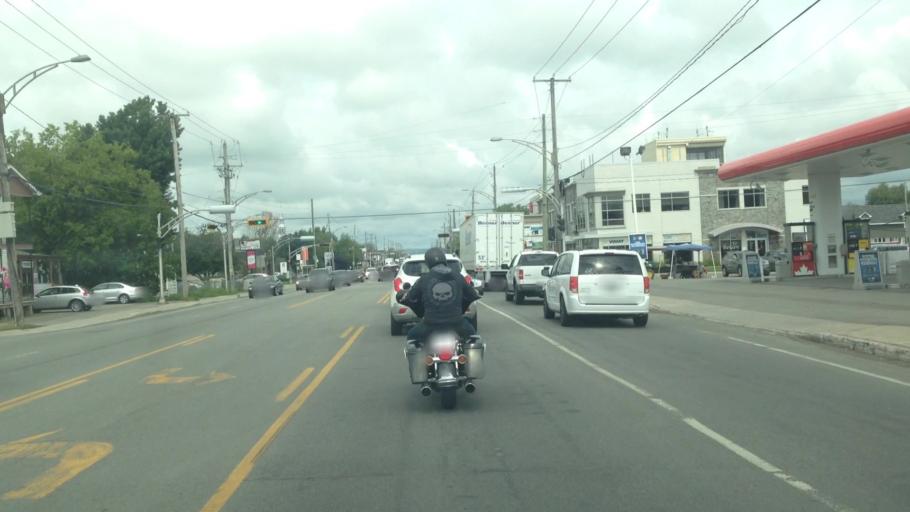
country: CA
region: Quebec
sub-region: Laurentides
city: Blainville
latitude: 45.7023
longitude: -73.9247
